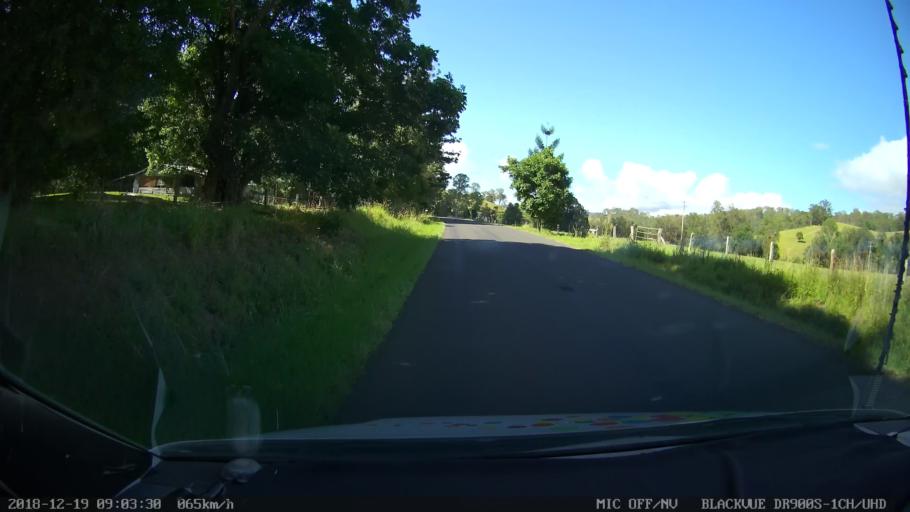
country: AU
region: New South Wales
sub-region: Kyogle
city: Kyogle
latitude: -28.4480
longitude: 152.9506
